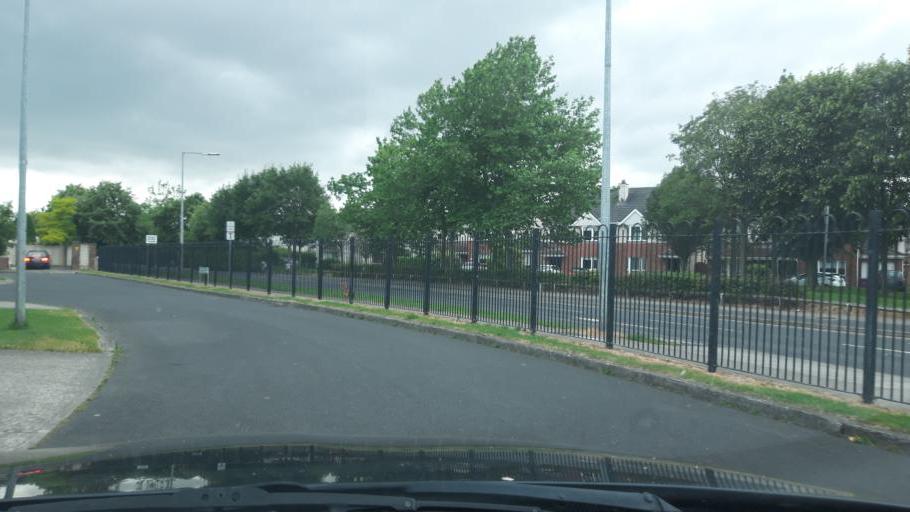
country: IE
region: Leinster
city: Hartstown
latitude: 53.4033
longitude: -6.4254
